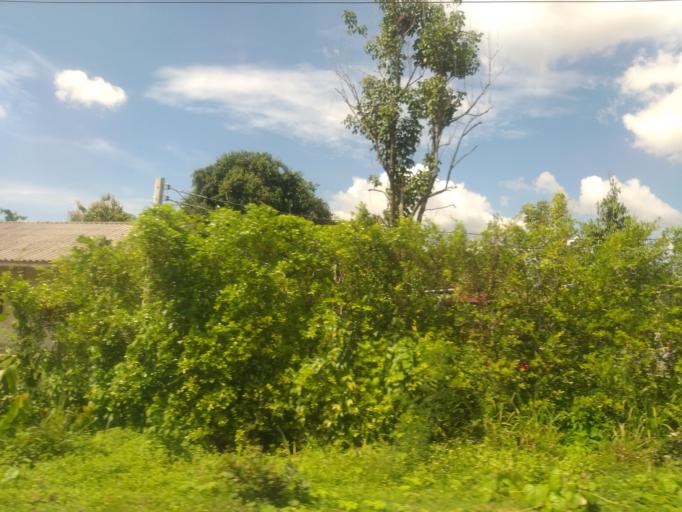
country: TH
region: Nakhon Nayok
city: Nakhon Nayok
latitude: 14.2737
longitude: 101.2897
